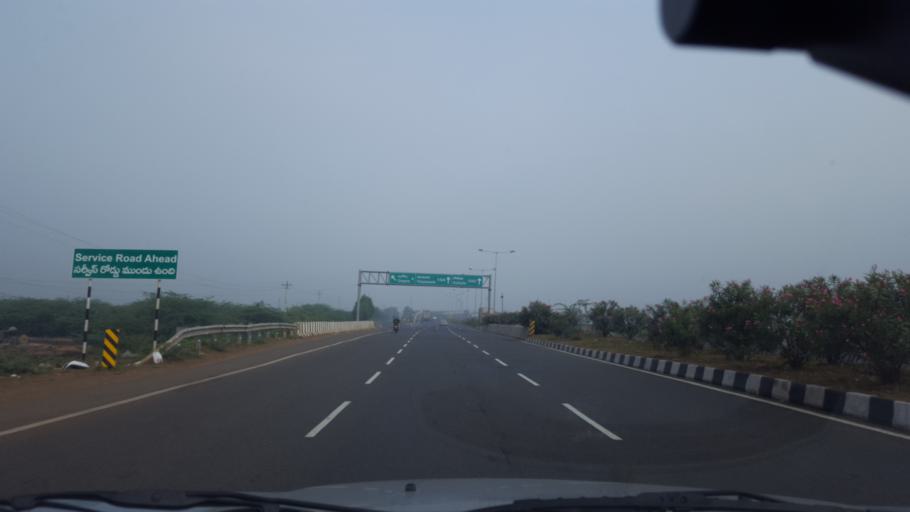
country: IN
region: Andhra Pradesh
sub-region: Prakasam
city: Ongole
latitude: 15.4649
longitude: 80.0481
